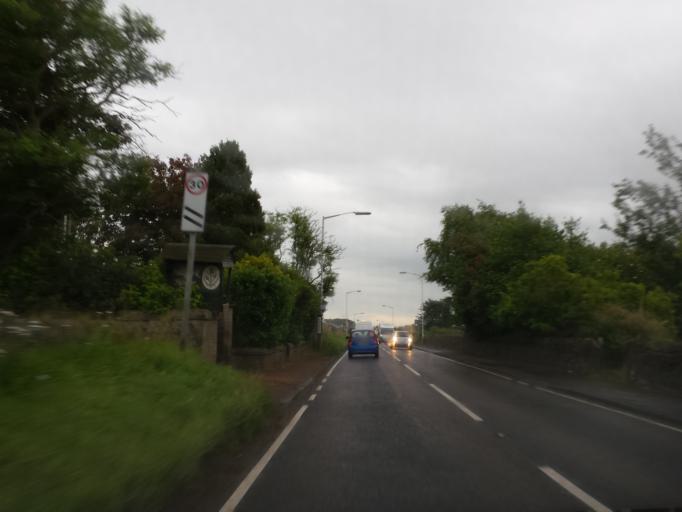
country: GB
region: Scotland
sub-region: Fife
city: Leuchars
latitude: 56.3852
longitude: -2.8927
